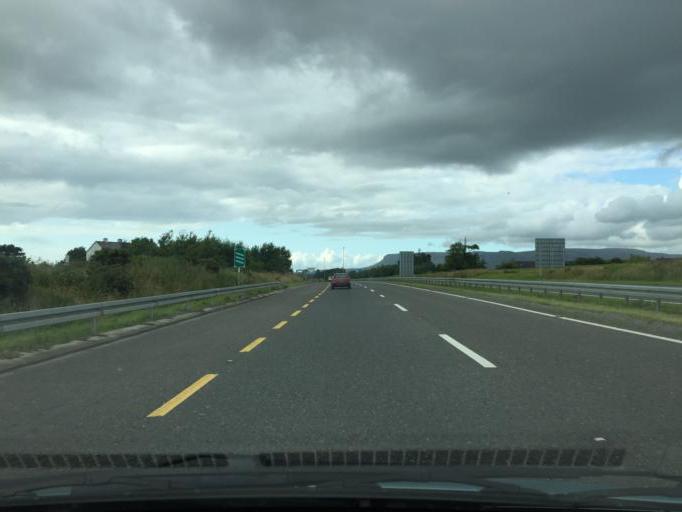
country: IE
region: Connaught
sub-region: Sligo
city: Sligo
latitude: 54.2528
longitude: -8.4775
